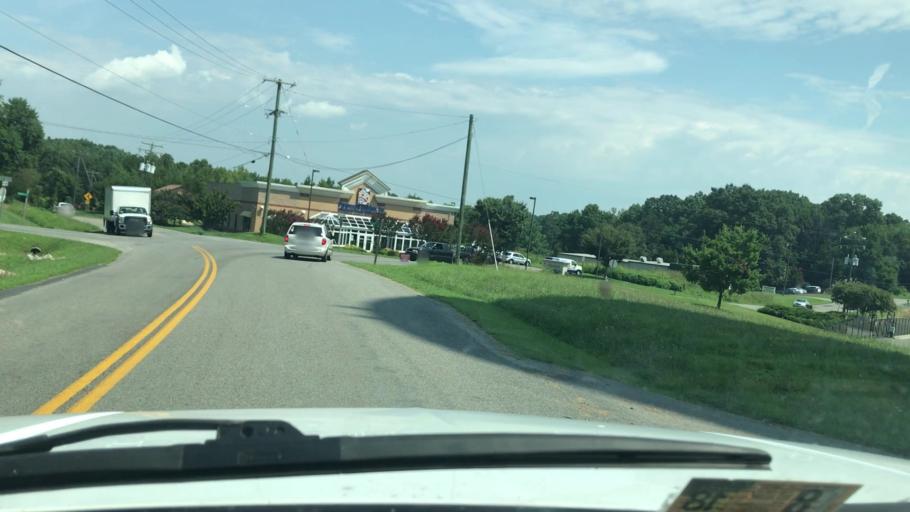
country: US
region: Virginia
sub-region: Henrico County
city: Short Pump
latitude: 37.6712
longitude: -77.6783
